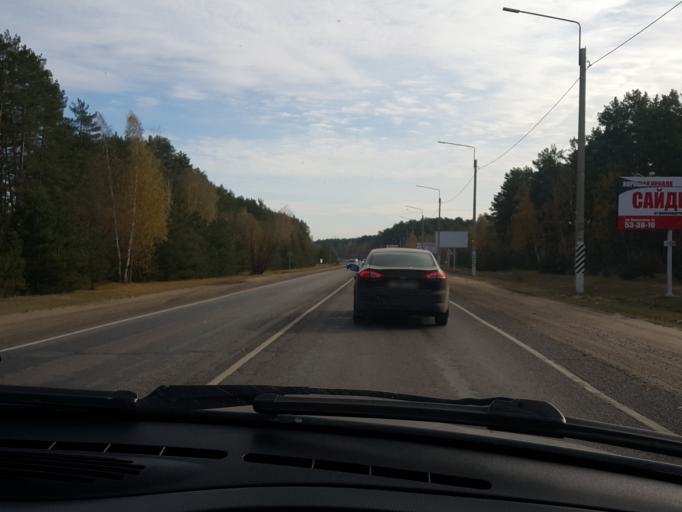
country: RU
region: Tambov
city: Donskoye
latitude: 52.7119
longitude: 41.5235
